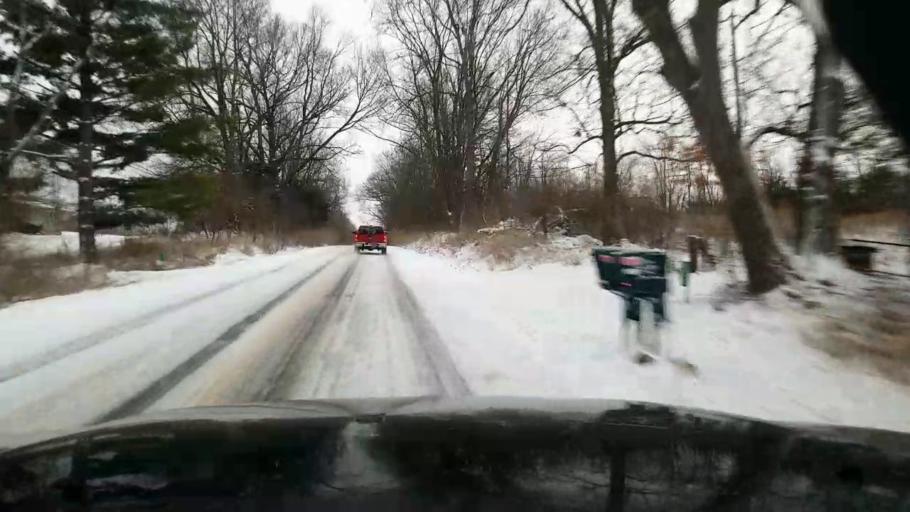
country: US
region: Michigan
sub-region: Jackson County
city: Spring Arbor
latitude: 42.1346
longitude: -84.4986
